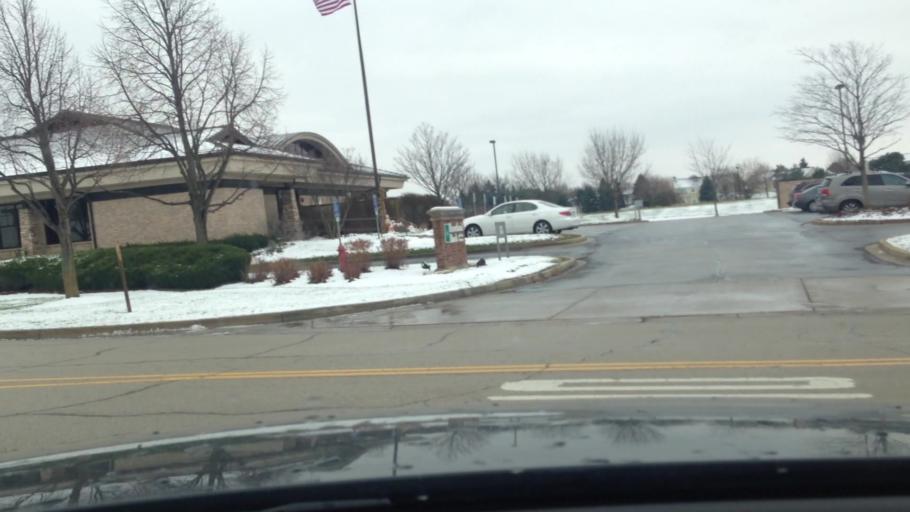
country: US
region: Illinois
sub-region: McHenry County
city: Huntley
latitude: 42.1486
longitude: -88.4341
